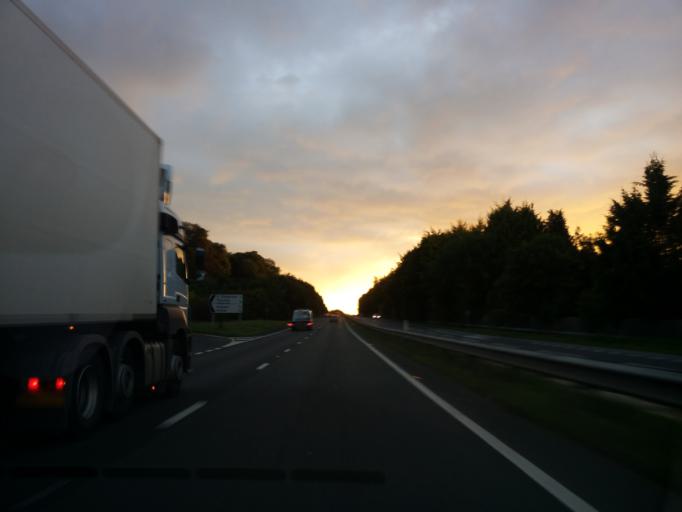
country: GB
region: England
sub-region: Hampshire
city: Abbotts Ann
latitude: 51.2096
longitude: -1.5776
